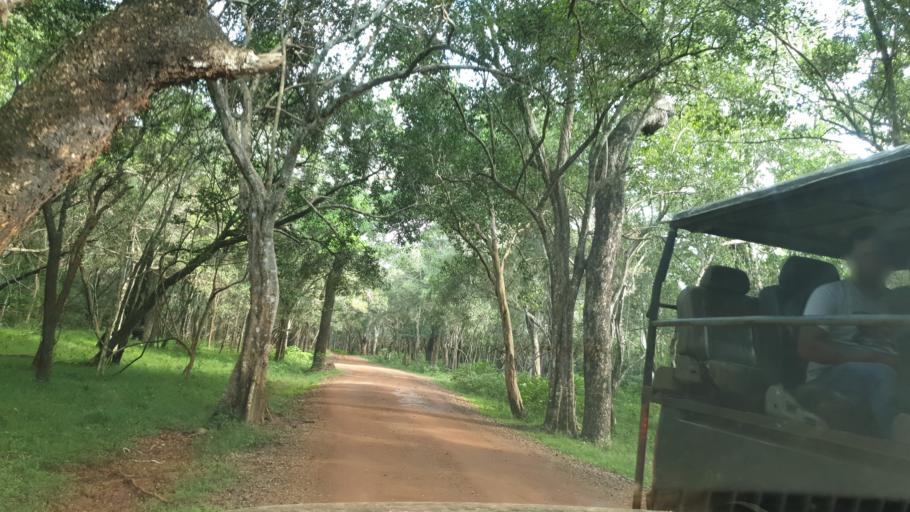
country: LK
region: North Central
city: Anuradhapura
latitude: 8.3810
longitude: 80.0643
